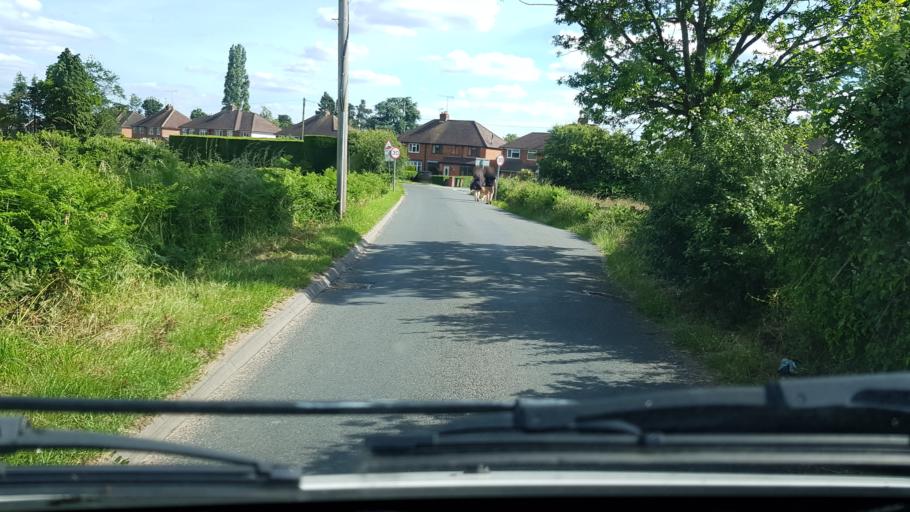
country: GB
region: England
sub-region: Worcestershire
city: Bewdley
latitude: 52.3848
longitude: -2.3016
